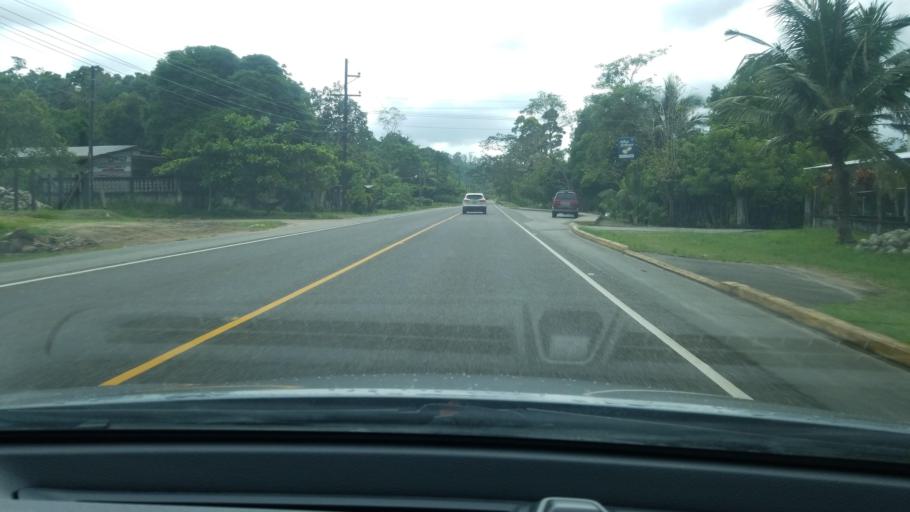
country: HN
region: Cortes
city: Potrerillos
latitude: 15.6111
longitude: -88.2848
